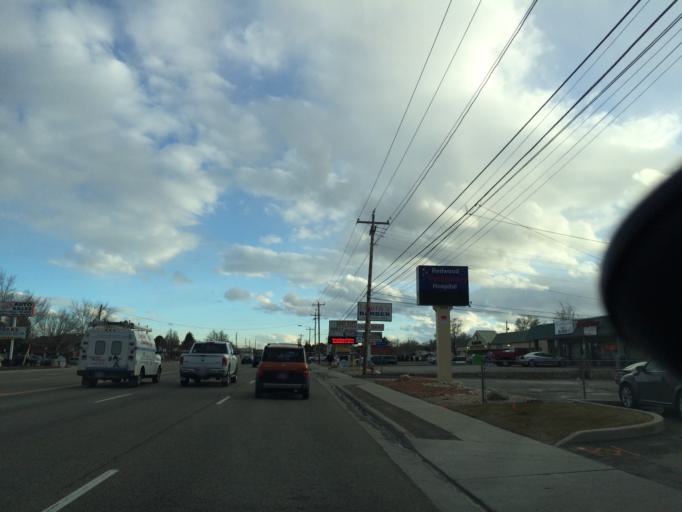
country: US
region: Utah
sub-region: Salt Lake County
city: Taylorsville
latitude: 40.6614
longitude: -111.9390
